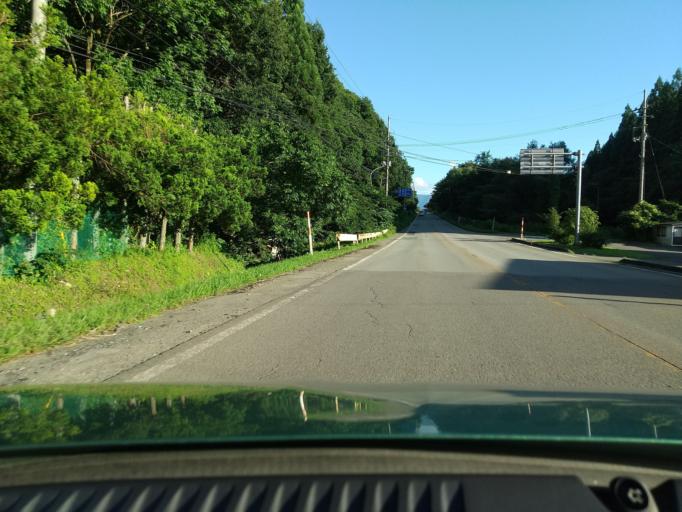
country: JP
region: Akita
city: Kakunodatemachi
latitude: 39.7365
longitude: 140.7179
